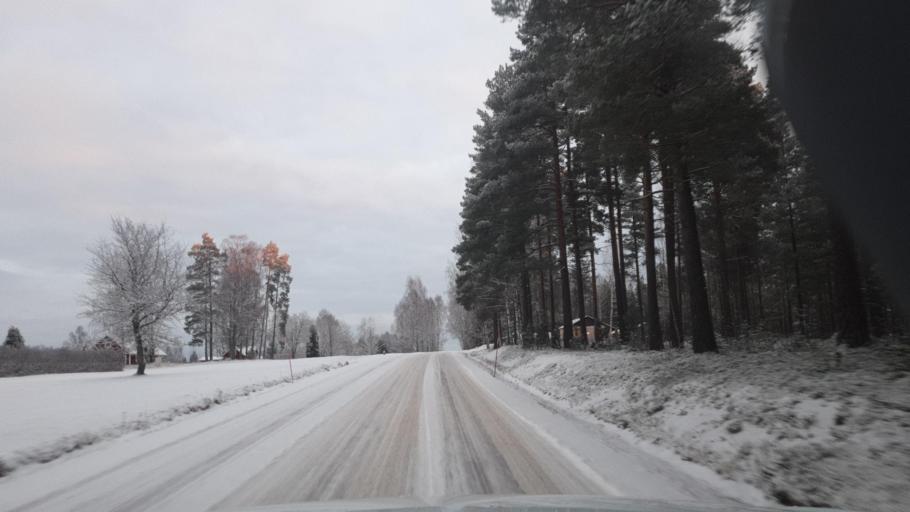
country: SE
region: Vaermland
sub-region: Eda Kommun
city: Charlottenberg
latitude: 59.7834
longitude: 12.2143
